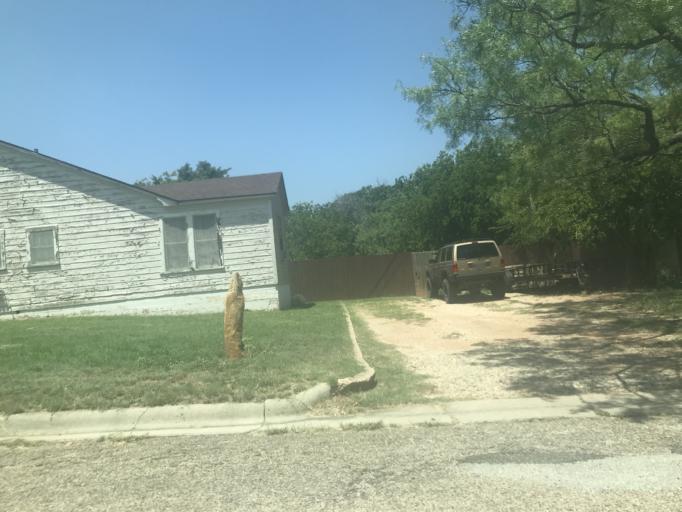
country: US
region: Texas
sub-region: Taylor County
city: Abilene
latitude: 32.4459
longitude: -99.7512
